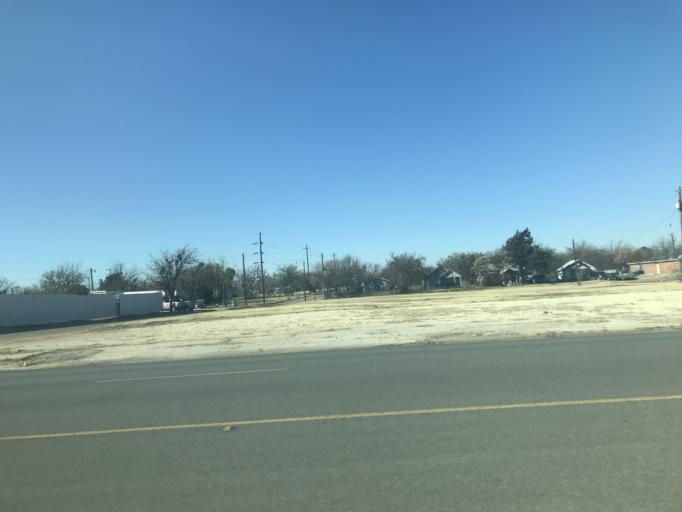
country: US
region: Texas
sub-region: Taylor County
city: Abilene
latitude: 32.4612
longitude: -99.7257
